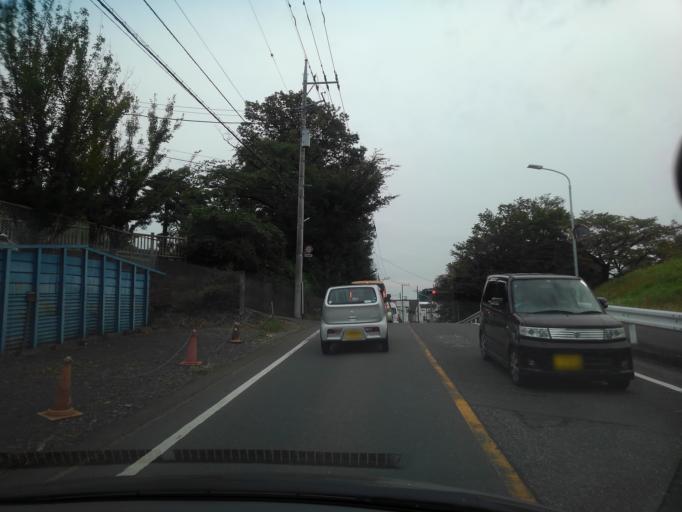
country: JP
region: Tokyo
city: Higashimurayama-shi
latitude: 35.7687
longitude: 139.4499
